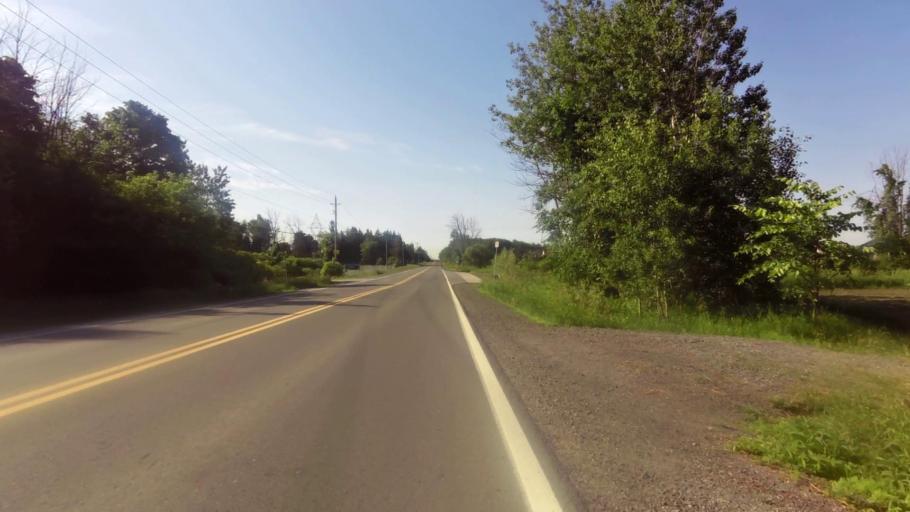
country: CA
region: Ontario
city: Ottawa
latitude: 45.2575
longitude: -75.5677
